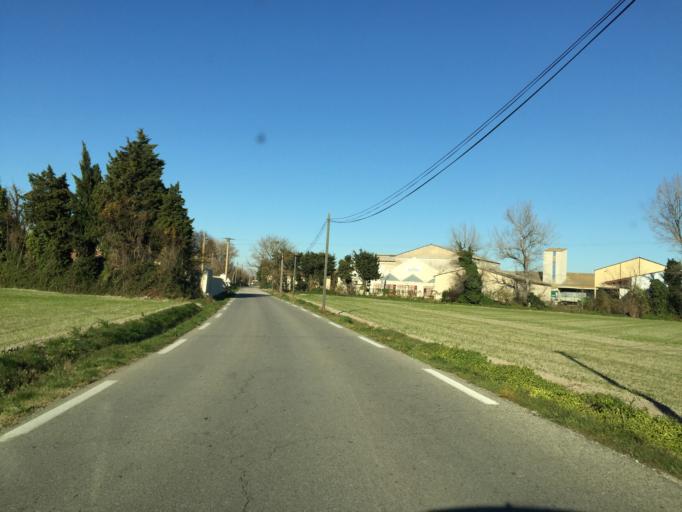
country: FR
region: Provence-Alpes-Cote d'Azur
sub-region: Departement du Vaucluse
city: Entraigues-sur-la-Sorgue
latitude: 44.0142
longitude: 4.9333
